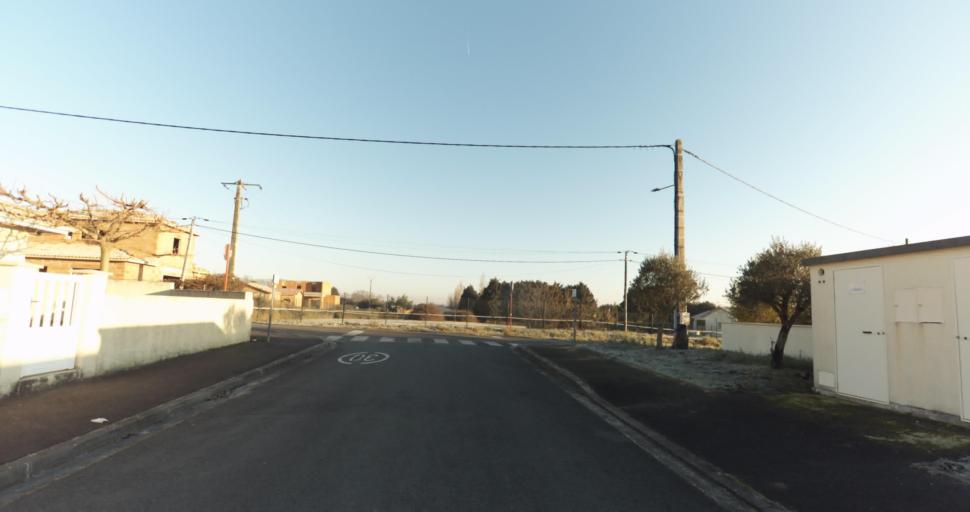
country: FR
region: Aquitaine
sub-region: Departement de la Gironde
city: Ambares-et-Lagrave
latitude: 44.9154
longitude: -0.4980
